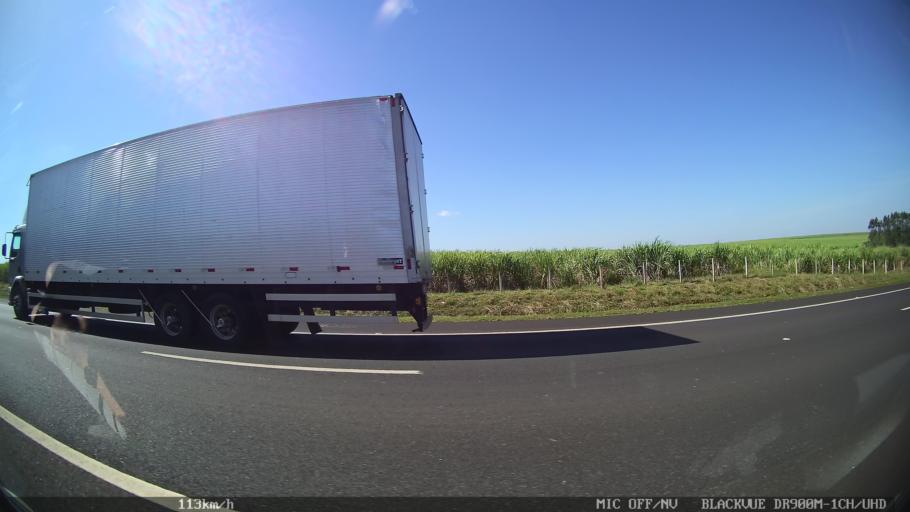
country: BR
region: Sao Paulo
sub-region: Franca
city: Franca
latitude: -20.6865
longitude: -47.4968
